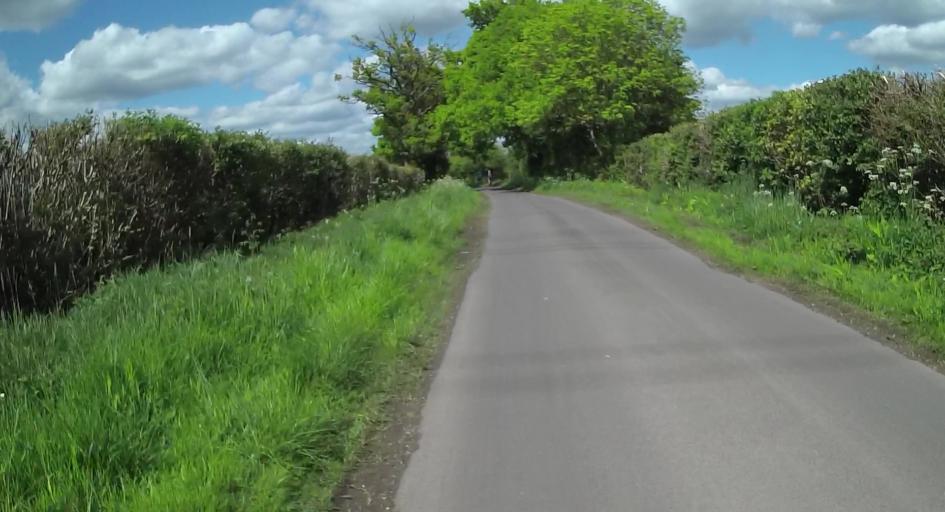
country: GB
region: England
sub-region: West Berkshire
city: Stratfield Mortimer
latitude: 51.3323
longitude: -1.0456
